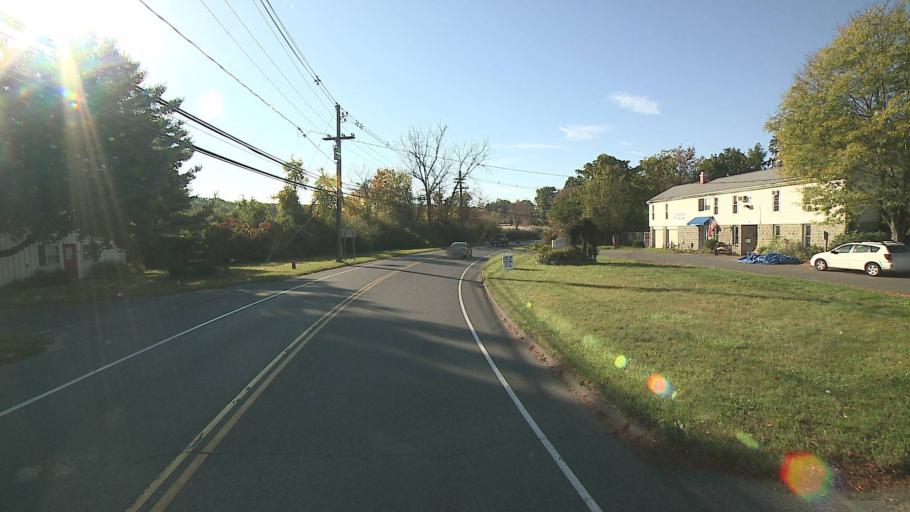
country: US
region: Connecticut
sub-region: Fairfield County
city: Bethel
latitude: 41.3638
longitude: -73.4209
